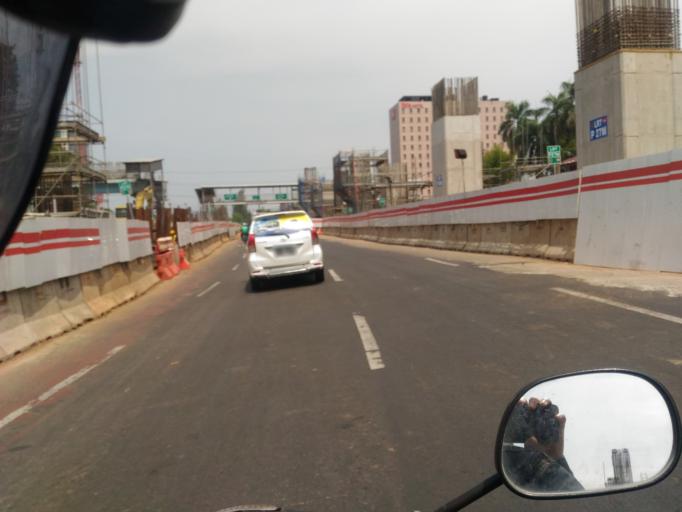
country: ID
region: Jakarta Raya
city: Jakarta
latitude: -6.2458
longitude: 106.8710
